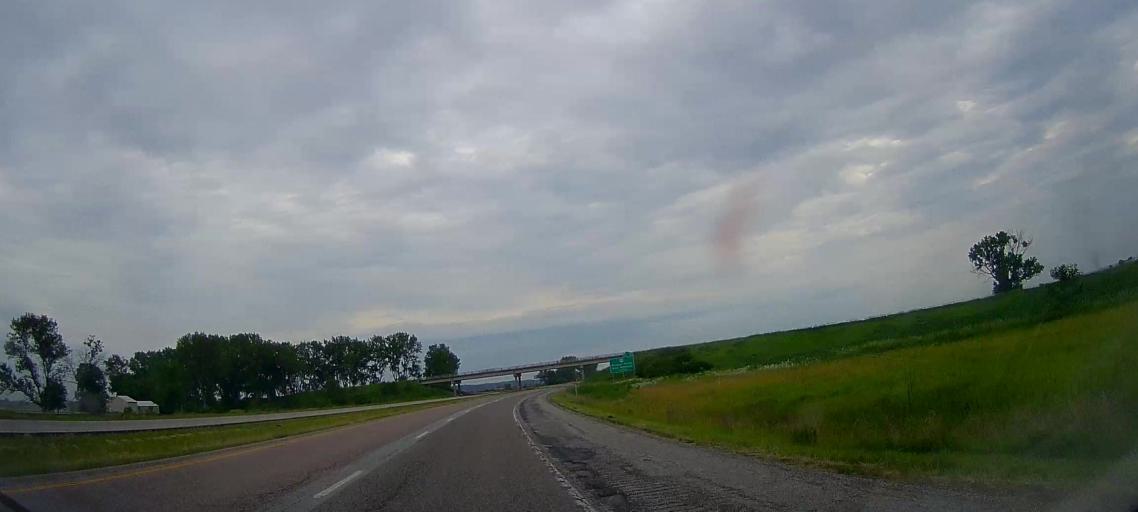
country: US
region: Iowa
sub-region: Harrison County
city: Missouri Valley
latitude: 41.5665
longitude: -95.9185
